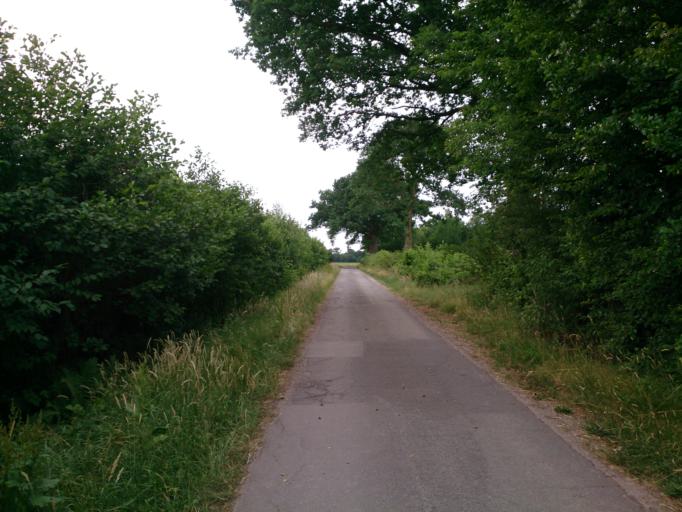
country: DE
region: Schleswig-Holstein
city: Hemdingen
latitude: 53.7362
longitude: 9.8088
